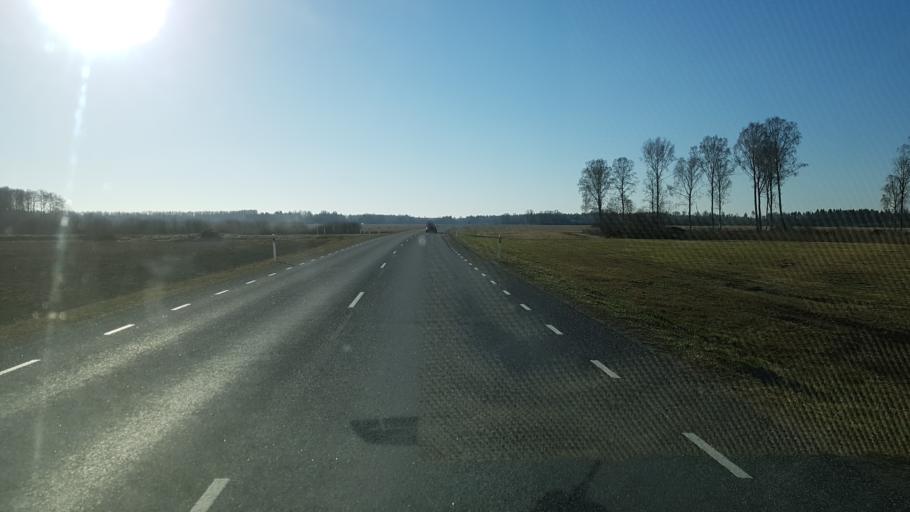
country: EE
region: Jaervamaa
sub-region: Tueri vald
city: Sarevere
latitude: 58.7754
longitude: 25.5095
